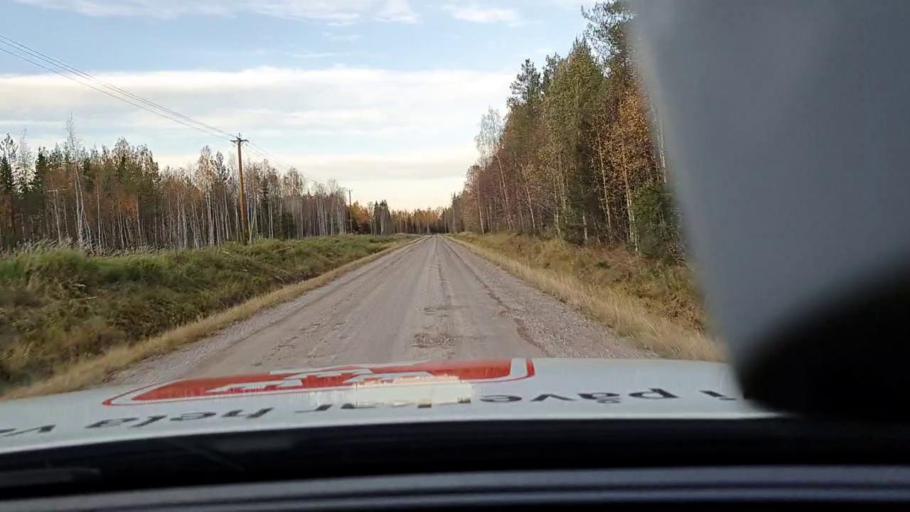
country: SE
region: Norrbotten
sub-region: Overkalix Kommun
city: OEverkalix
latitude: 66.3245
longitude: 22.5406
